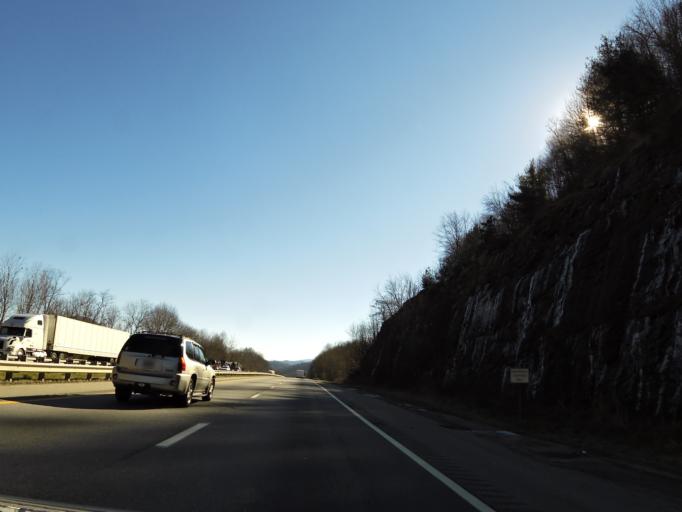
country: US
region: North Carolina
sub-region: Haywood County
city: Cove Creek
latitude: 35.5805
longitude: -82.9864
